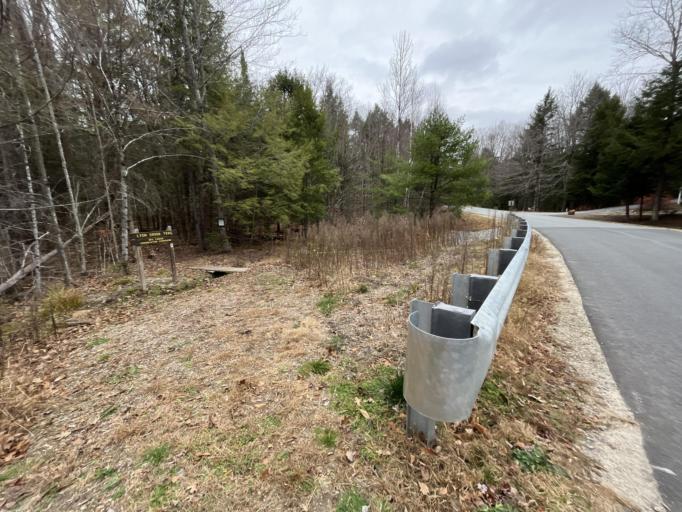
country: US
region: New Hampshire
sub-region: Merrimack County
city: New London
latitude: 43.3974
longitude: -71.9739
